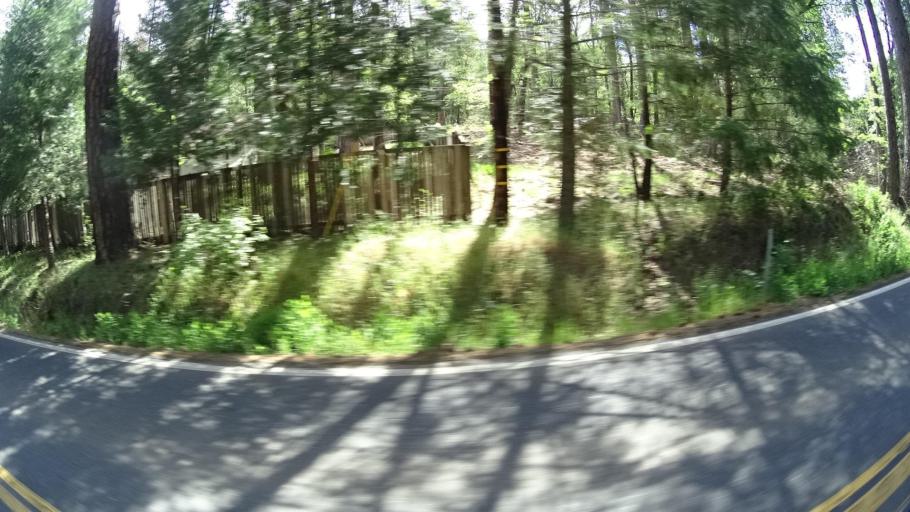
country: US
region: California
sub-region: Lake County
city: Cobb
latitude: 38.8642
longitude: -122.7186
